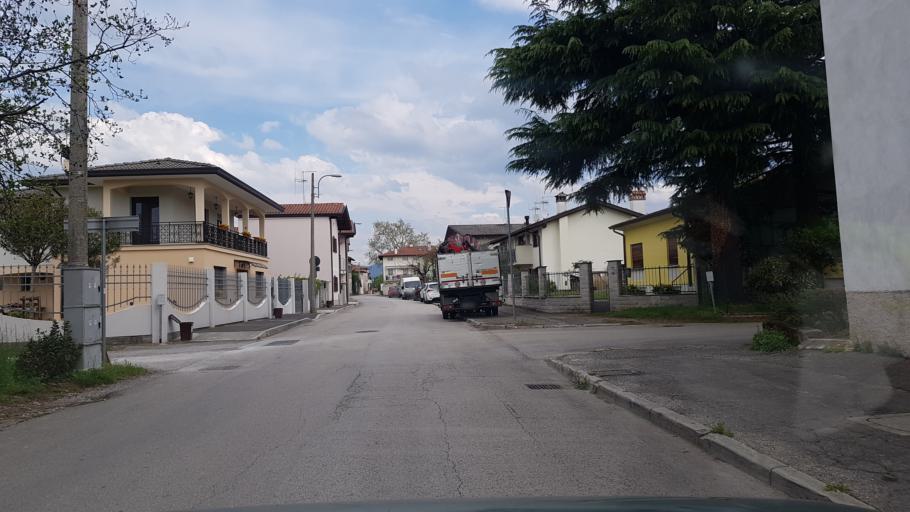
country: SI
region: Miren-Kostanjevica
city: Miren
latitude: 45.9175
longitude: 13.6008
